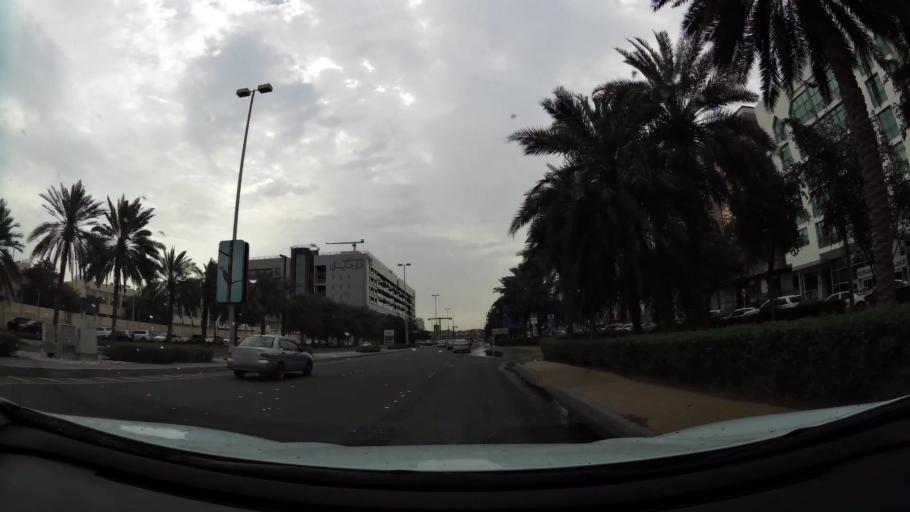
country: AE
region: Abu Dhabi
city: Abu Dhabi
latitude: 24.4802
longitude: 54.3790
